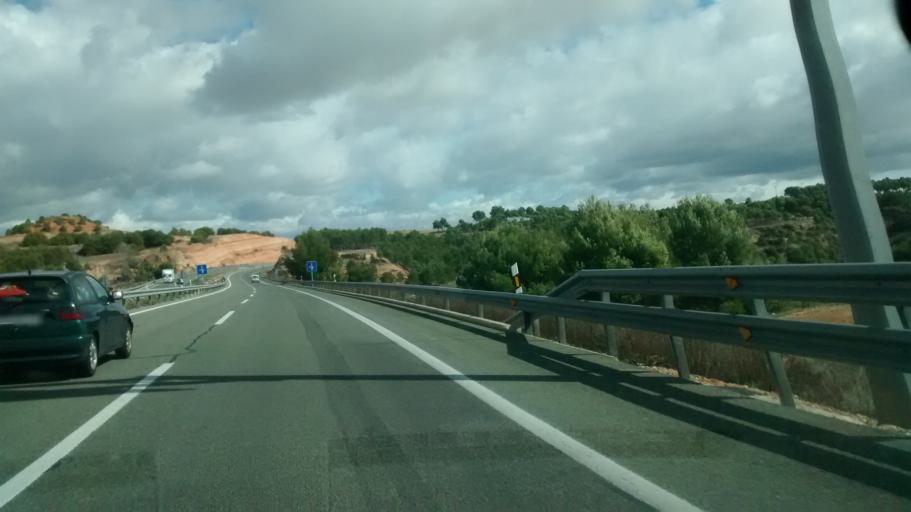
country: ES
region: Aragon
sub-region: Provincia de Zaragoza
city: Ariza
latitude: 41.3164
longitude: -2.0644
